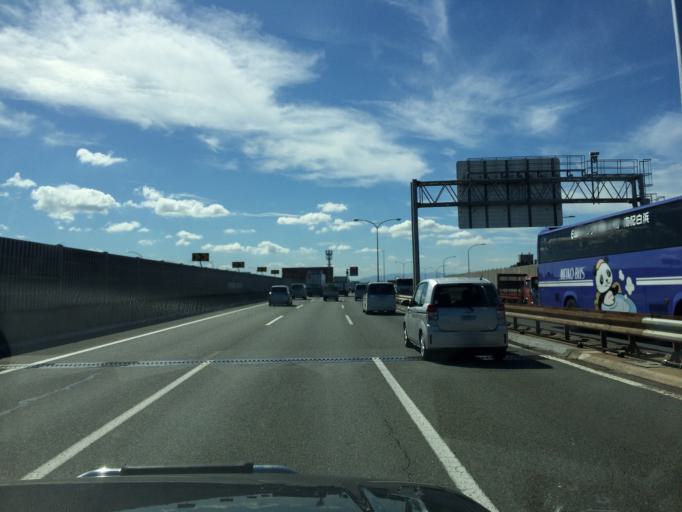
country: JP
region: Osaka
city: Yao
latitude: 34.6568
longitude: 135.5987
